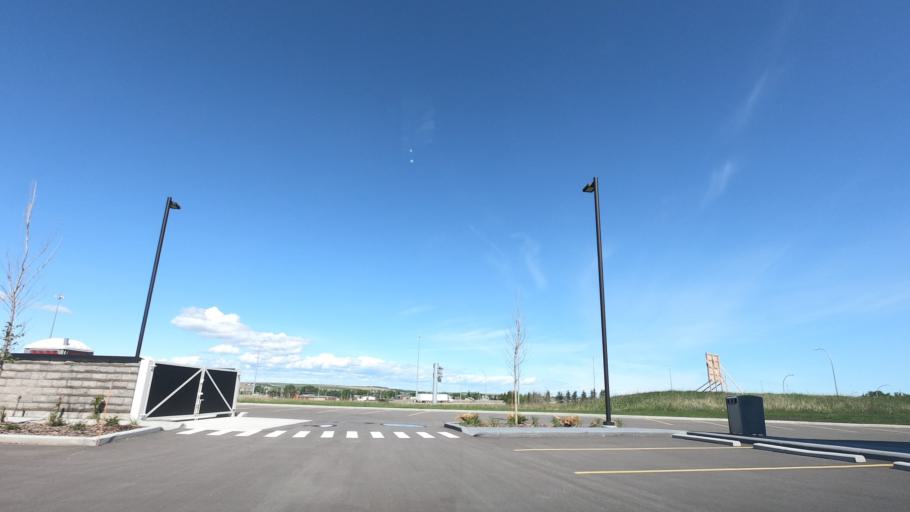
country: CA
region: Alberta
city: Airdrie
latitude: 51.2685
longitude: -113.9987
